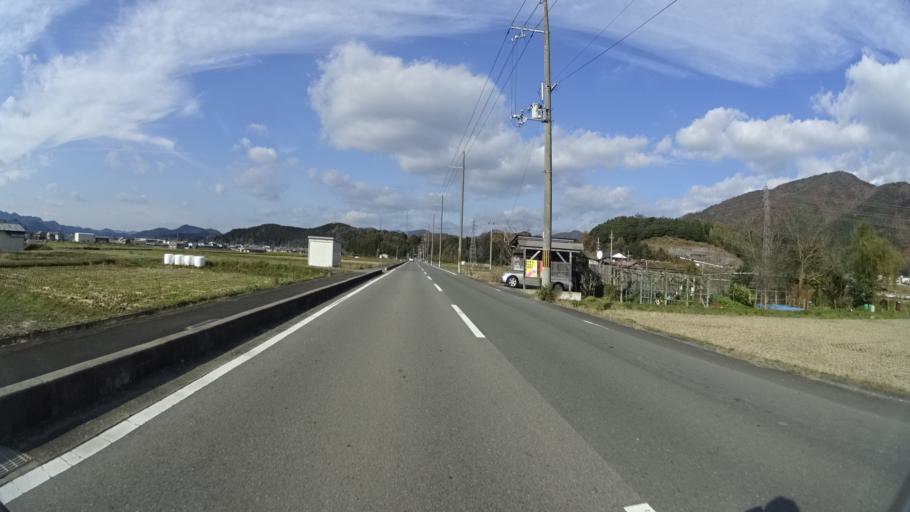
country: JP
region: Kyoto
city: Kameoka
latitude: 35.0591
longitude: 135.5684
